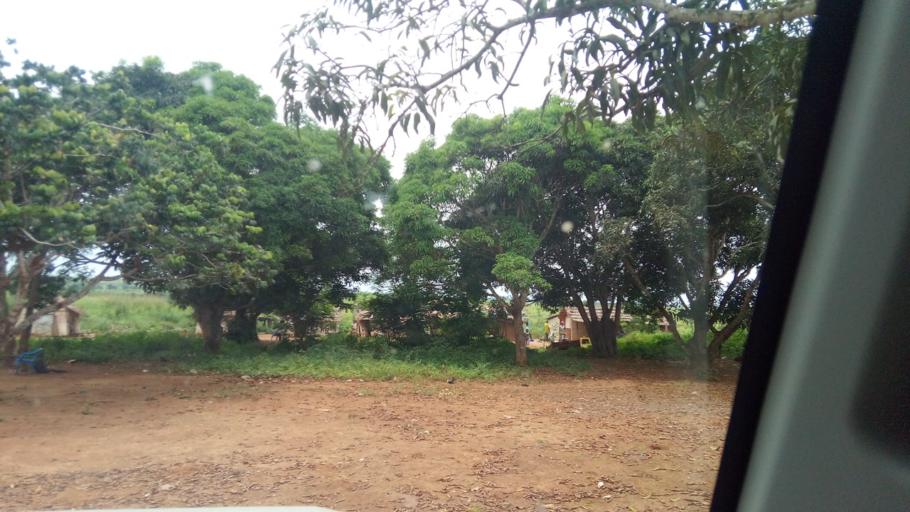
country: AO
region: Zaire
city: Mbanza Congo
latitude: -5.8276
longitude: 14.0557
